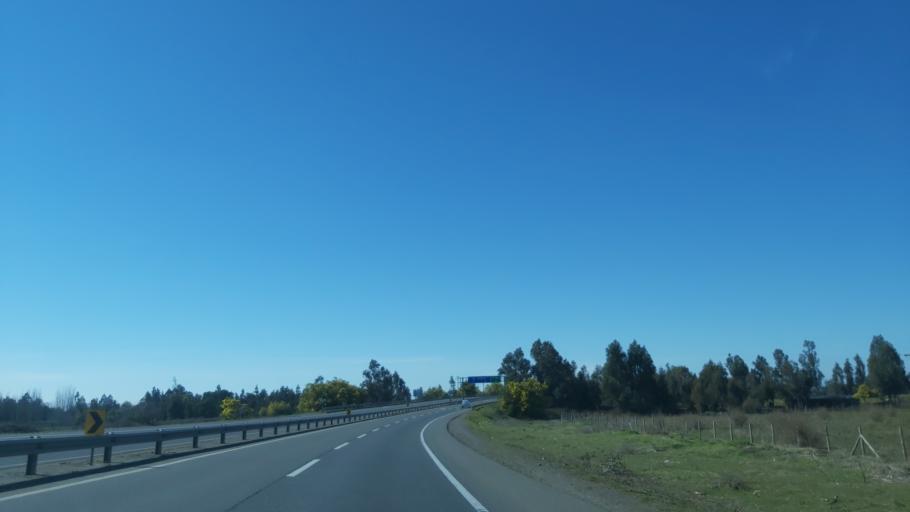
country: CL
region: Biobio
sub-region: Provincia de Nuble
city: Bulnes
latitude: -36.6537
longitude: -72.2367
